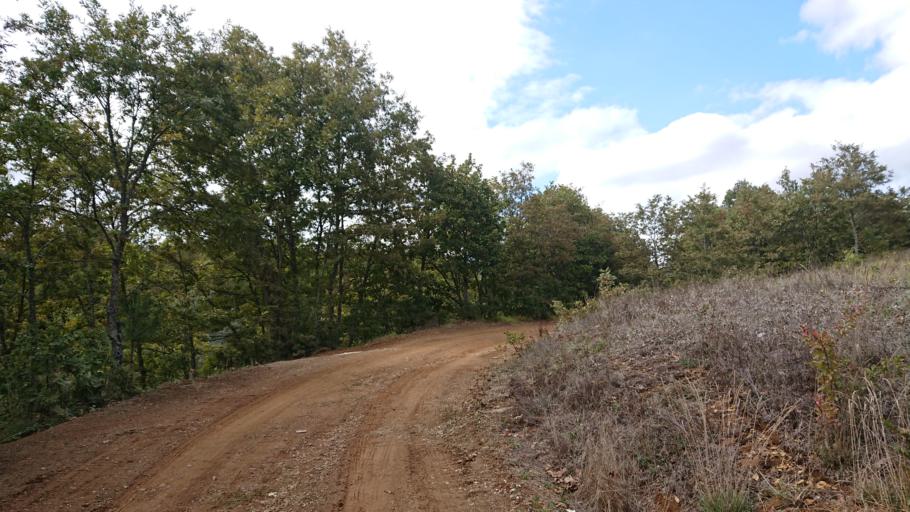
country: TR
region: Bilecik
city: Pazaryeri
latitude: 40.0181
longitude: 29.7906
